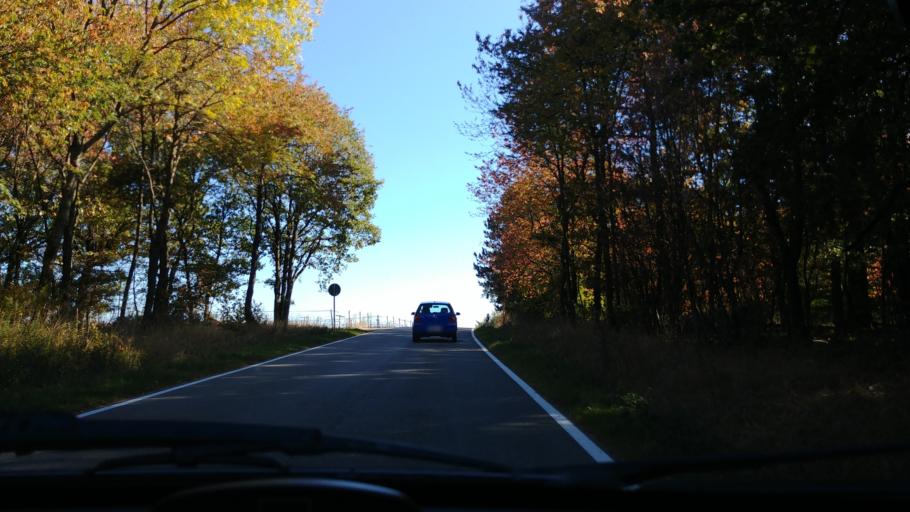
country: DE
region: Hesse
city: Taunusstein
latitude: 50.1635
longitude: 8.1183
